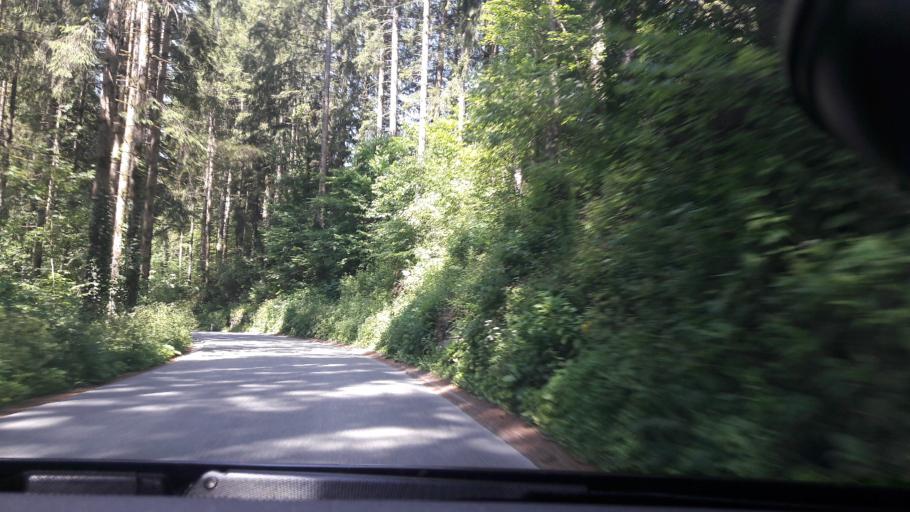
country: AT
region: Styria
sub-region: Politischer Bezirk Voitsberg
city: Kohlschwarz
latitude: 47.1150
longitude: 15.1340
